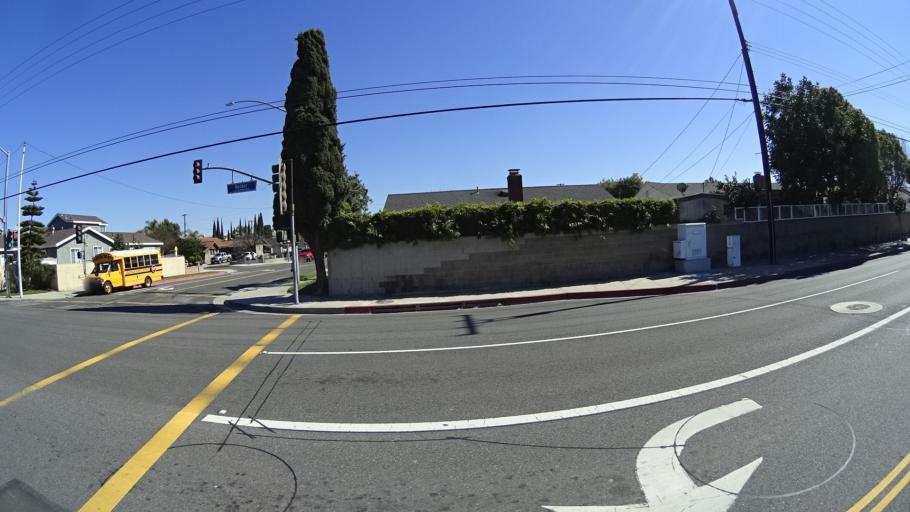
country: US
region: California
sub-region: Orange County
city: Cypress
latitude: 33.8278
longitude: -118.0197
